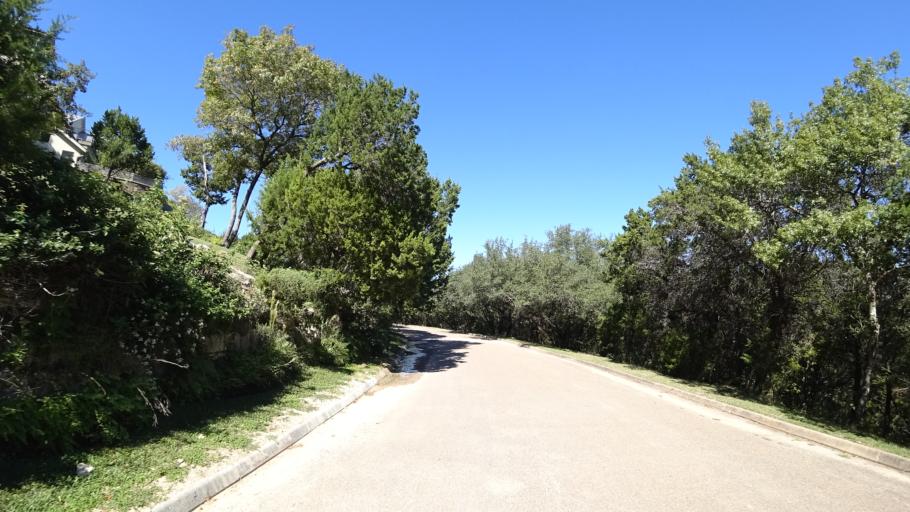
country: US
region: Texas
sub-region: Travis County
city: West Lake Hills
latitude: 30.3154
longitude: -97.7912
